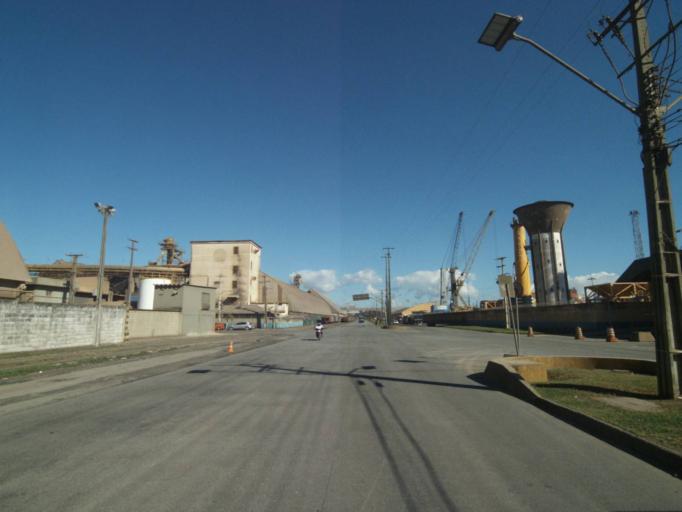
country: BR
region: Parana
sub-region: Paranagua
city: Paranagua
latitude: -25.5034
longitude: -48.5091
